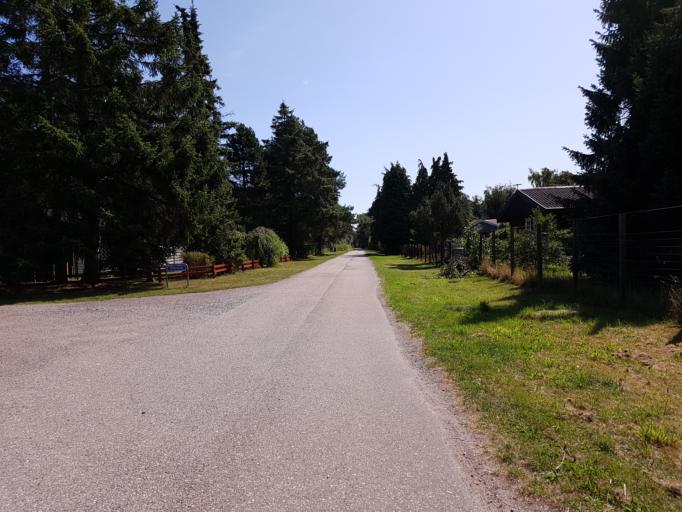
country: DK
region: Zealand
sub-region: Guldborgsund Kommune
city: Nykobing Falster
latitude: 54.5949
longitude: 11.9610
